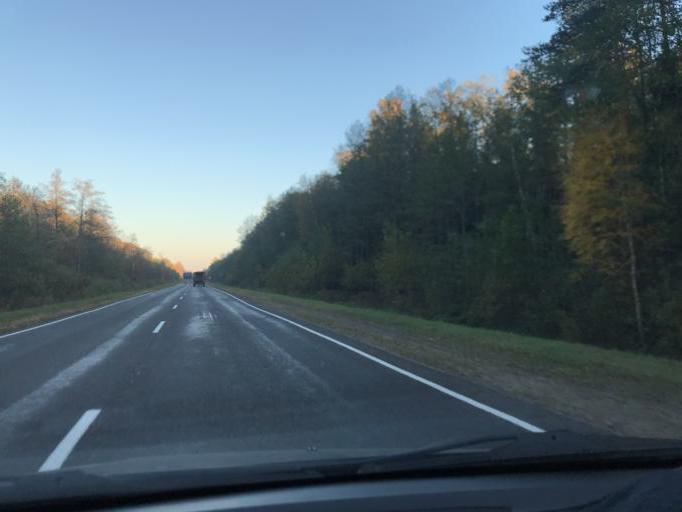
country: BY
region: Minsk
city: Staryya Darohi
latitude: 53.0435
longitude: 28.1378
